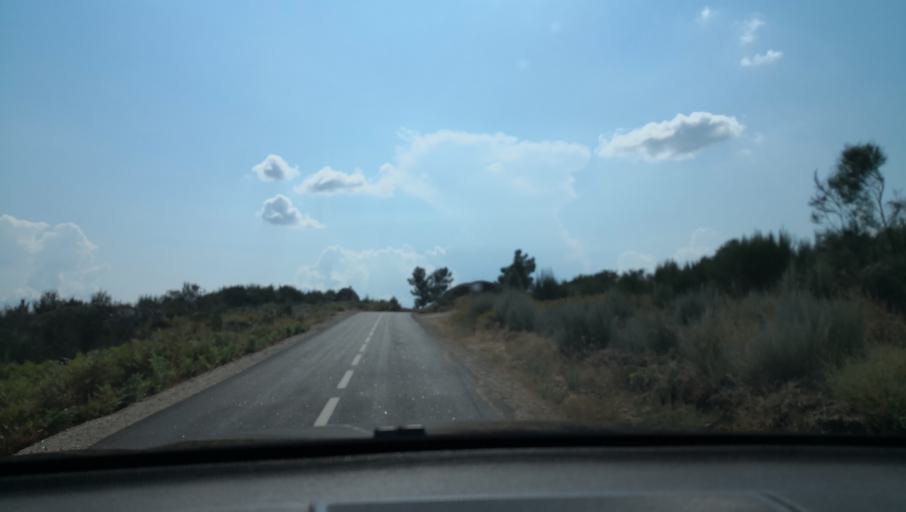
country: PT
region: Vila Real
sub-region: Sabrosa
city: Sabrosa
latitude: 41.2909
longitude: -7.6128
